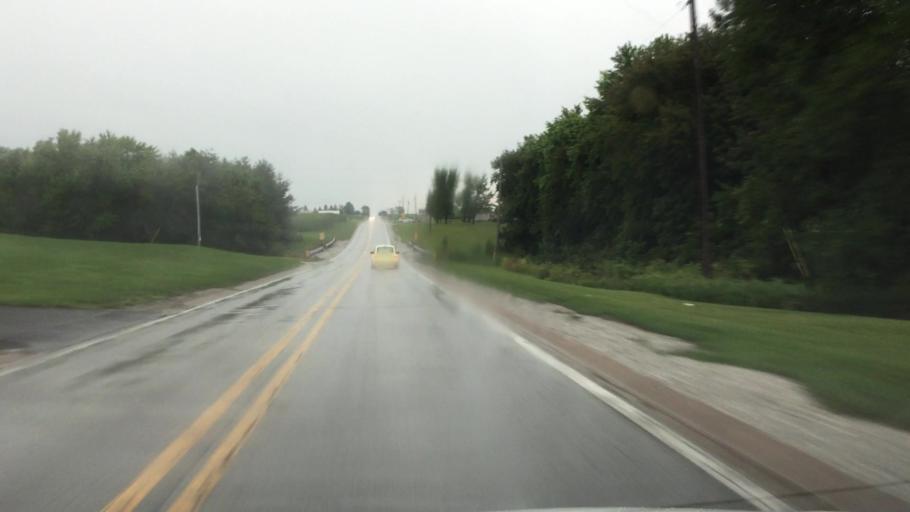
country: US
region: Illinois
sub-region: Hancock County
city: Carthage
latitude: 40.4572
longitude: -91.1396
